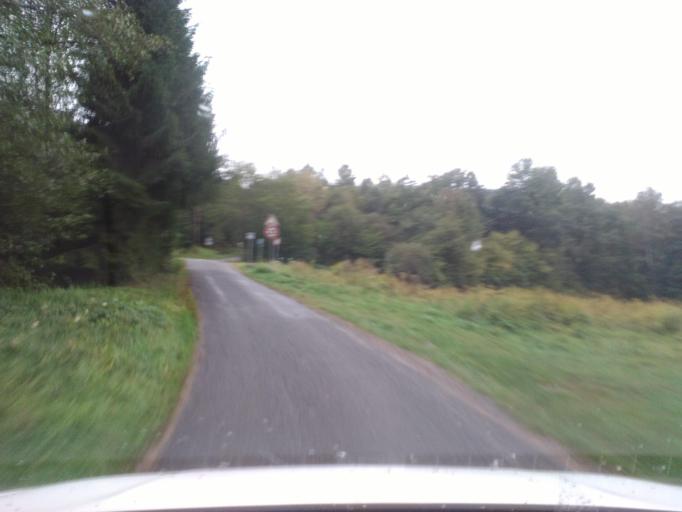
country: FR
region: Lorraine
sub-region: Departement des Vosges
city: Senones
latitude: 48.3835
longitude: 6.9445
